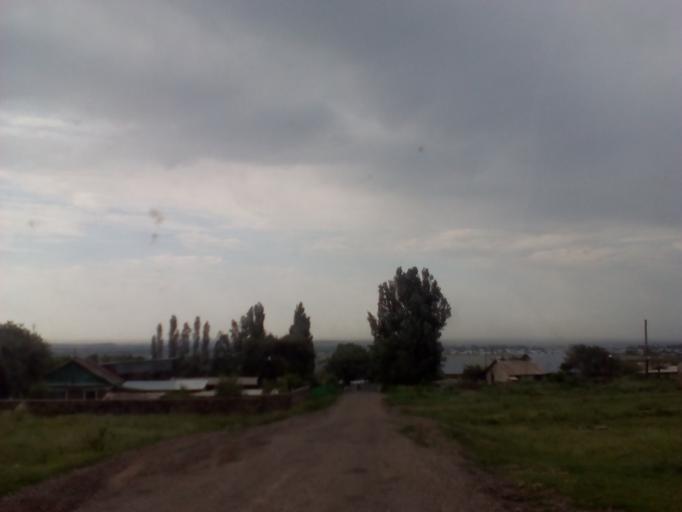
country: KZ
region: Almaty Oblysy
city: Burunday
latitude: 43.1523
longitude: 76.3851
